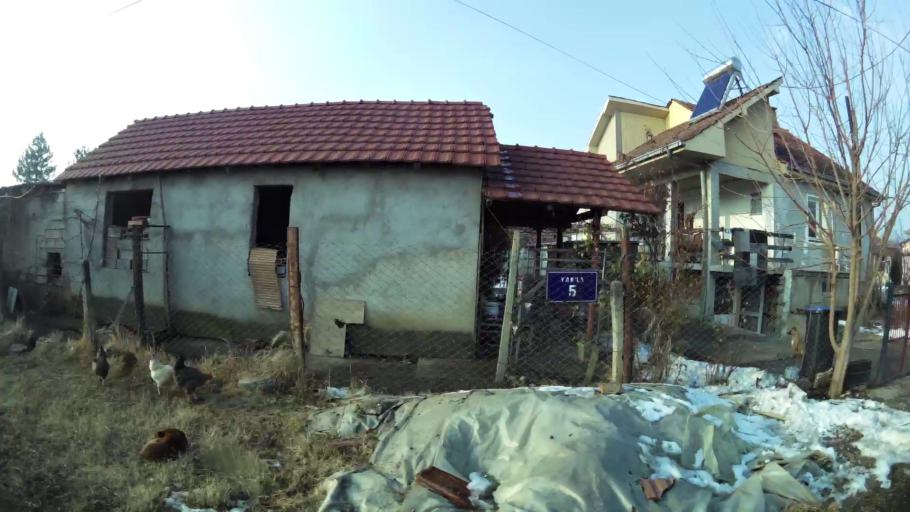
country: MK
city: Miladinovci
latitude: 41.9751
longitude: 21.6468
